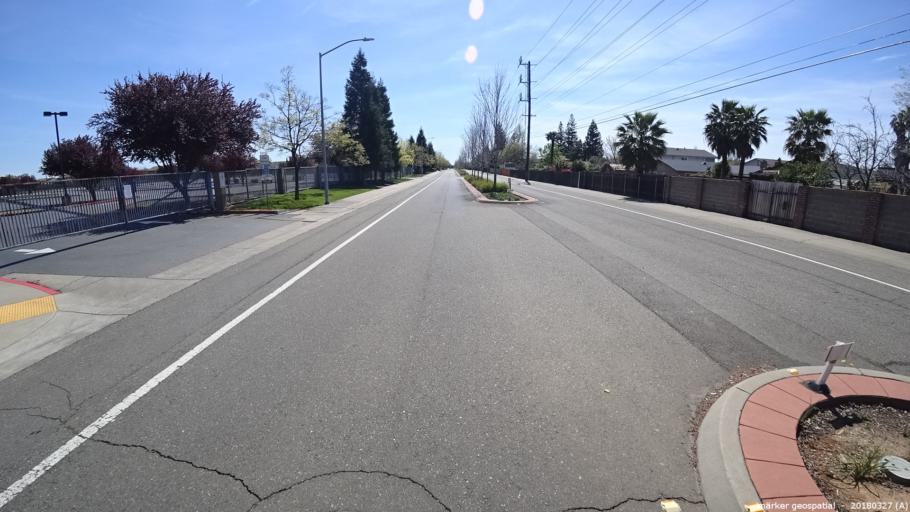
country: US
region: California
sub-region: Sacramento County
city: Rosemont
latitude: 38.5434
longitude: -121.3440
